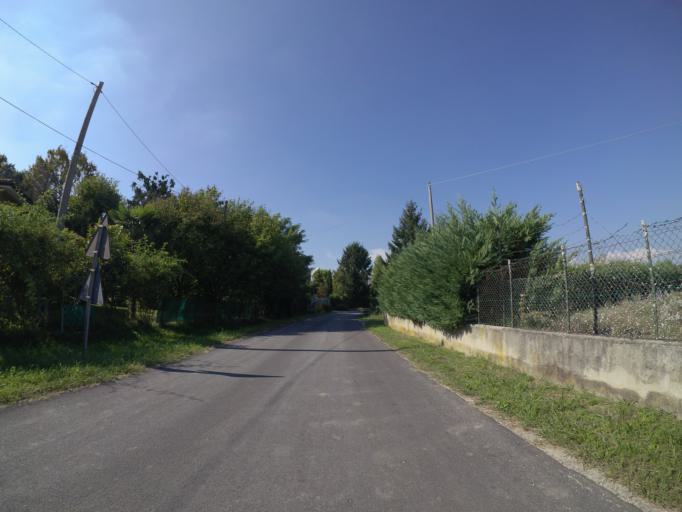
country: IT
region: Friuli Venezia Giulia
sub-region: Provincia di Udine
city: Muzzana del Turgnano
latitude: 45.8183
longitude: 13.1180
